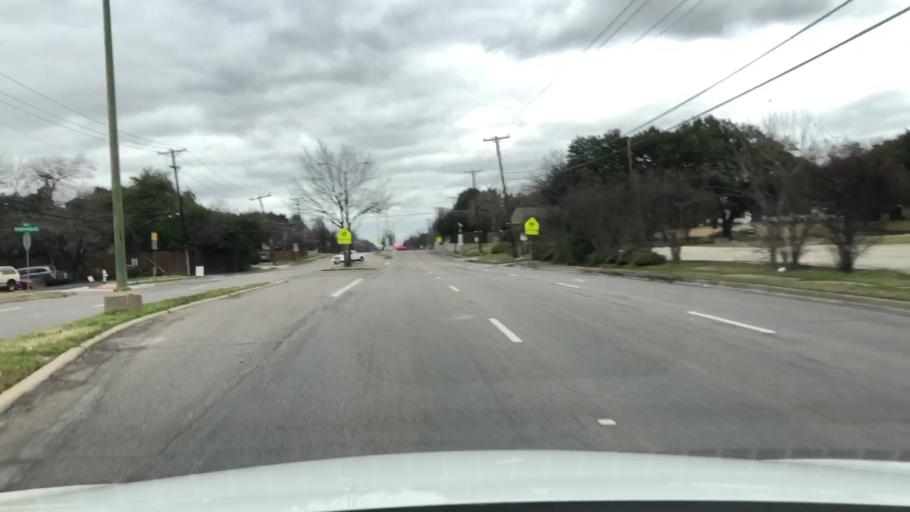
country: US
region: Texas
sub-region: Dallas County
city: Farmers Branch
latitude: 32.9113
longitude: -96.8559
